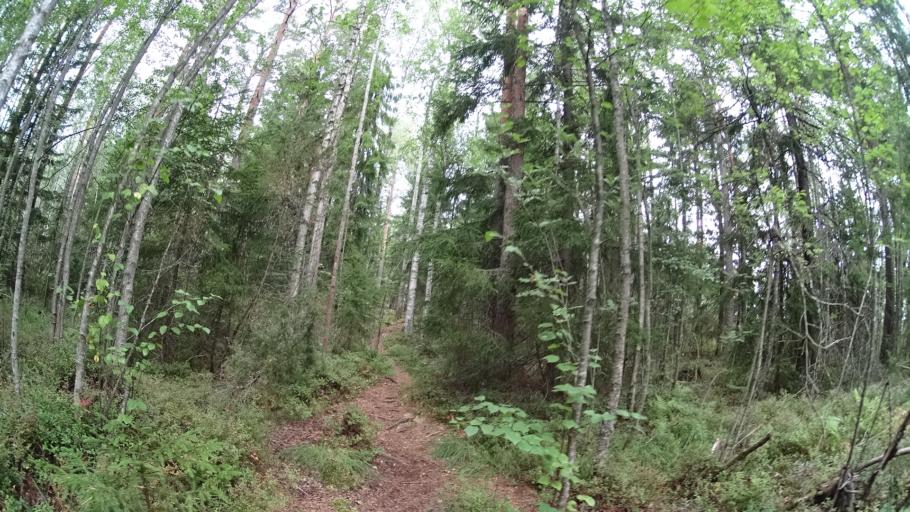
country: FI
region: Uusimaa
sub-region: Helsinki
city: Espoo
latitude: 60.3077
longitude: 24.5793
